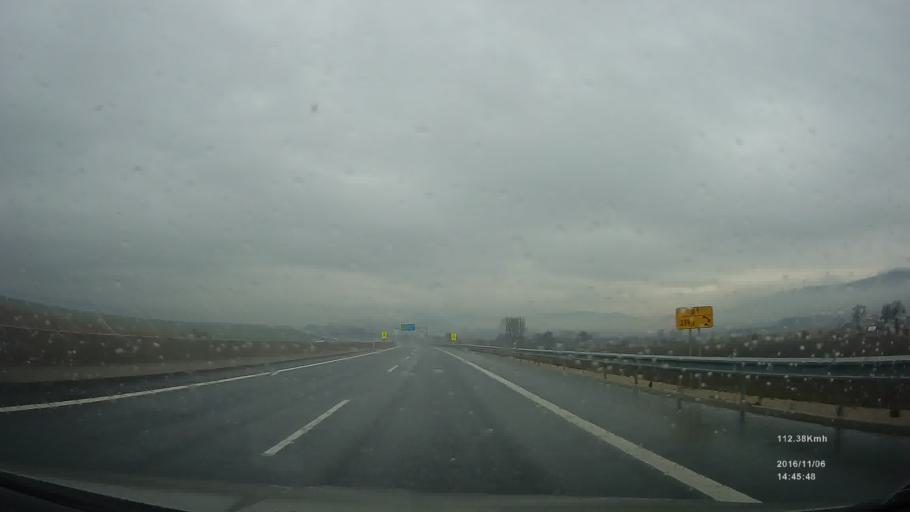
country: SK
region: Presovsky
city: Spisske Podhradie
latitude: 49.0066
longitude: 20.6862
